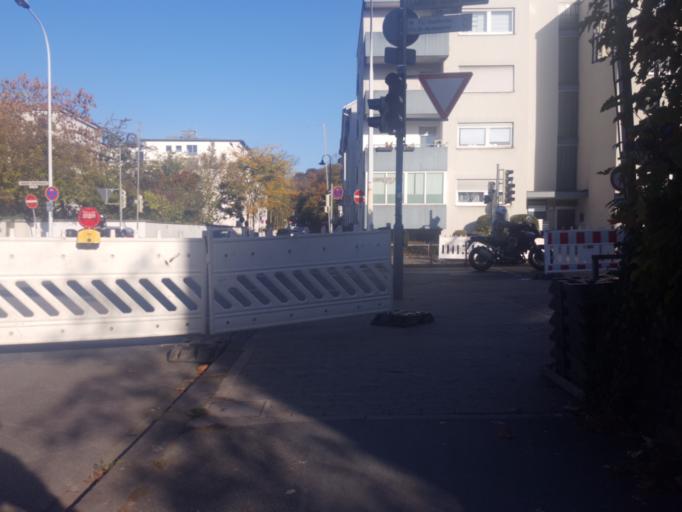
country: DE
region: Hesse
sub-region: Regierungsbezirk Darmstadt
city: Darmstadt
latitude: 49.8732
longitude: 8.6674
